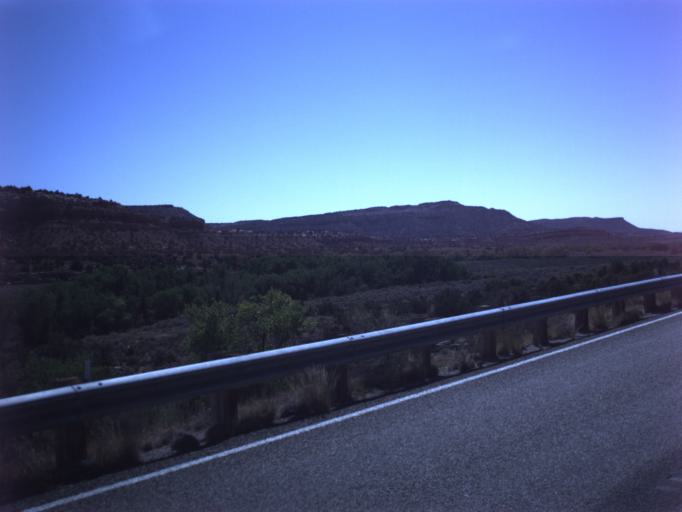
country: US
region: Utah
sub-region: San Juan County
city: Blanding
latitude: 37.4994
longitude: -109.6364
